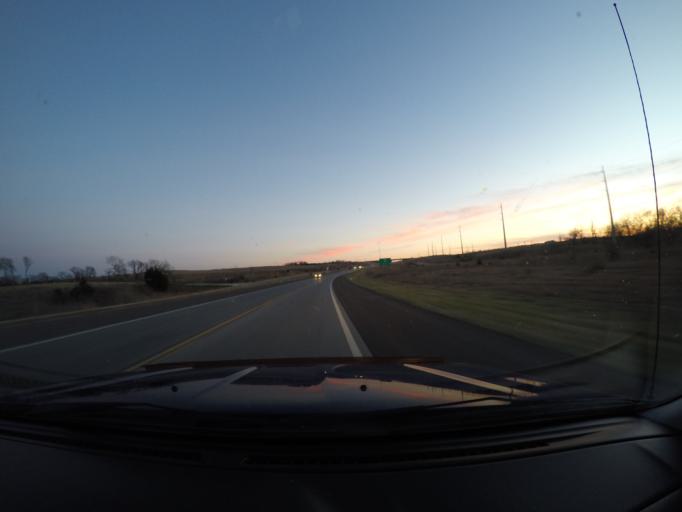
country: US
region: Kansas
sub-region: Douglas County
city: Lawrence
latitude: 38.9800
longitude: -95.3350
